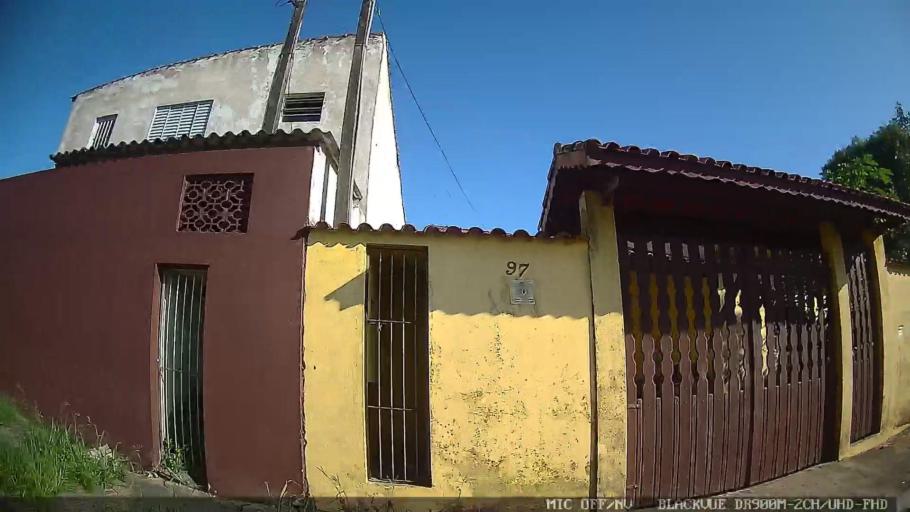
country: BR
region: Sao Paulo
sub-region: Peruibe
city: Peruibe
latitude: -24.2743
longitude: -46.9515
